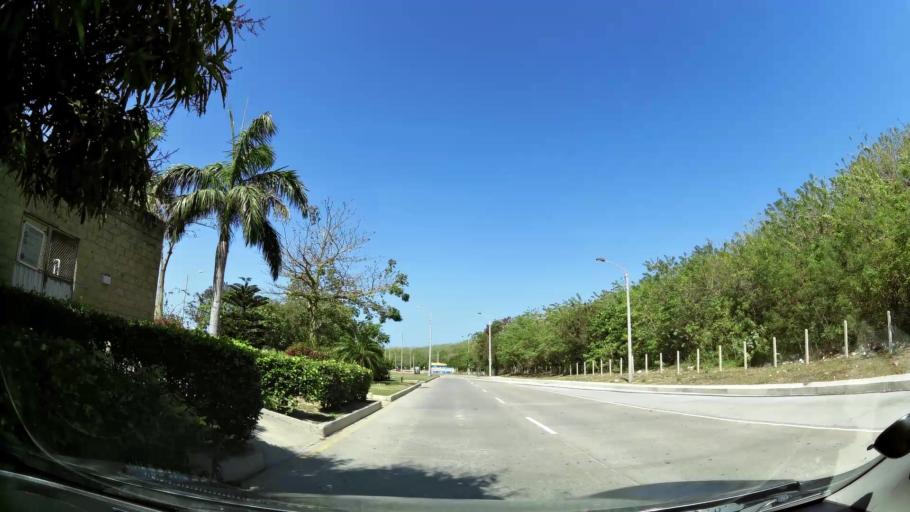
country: CO
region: Atlantico
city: Barranquilla
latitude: 11.0206
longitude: -74.8392
